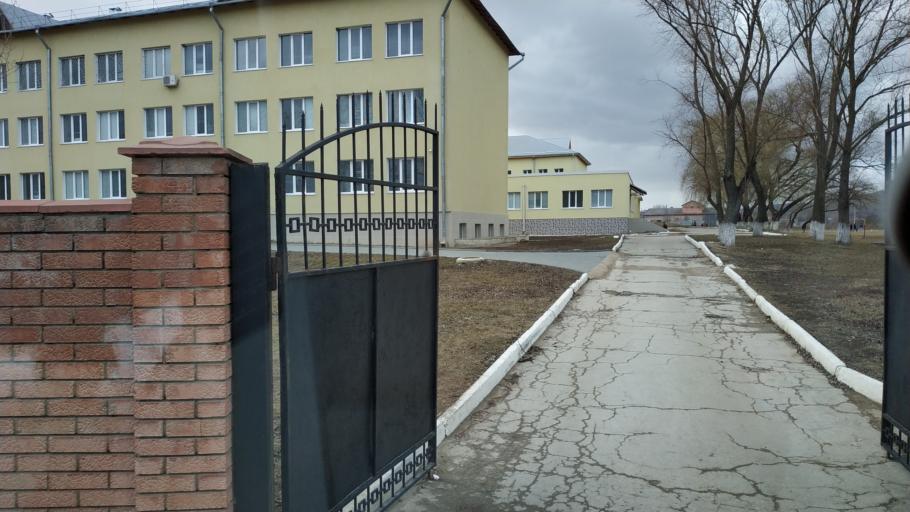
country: MD
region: Calarasi
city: Calarasi
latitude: 47.2825
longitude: 28.1976
